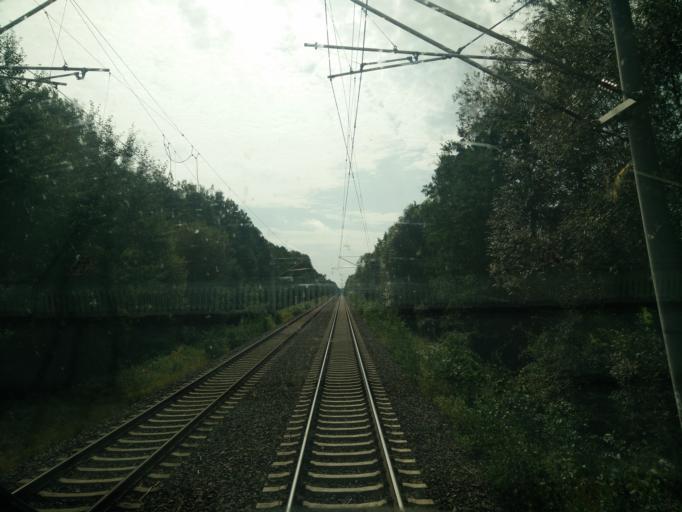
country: DE
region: Brandenburg
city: Luebben
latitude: 51.9029
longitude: 13.9049
